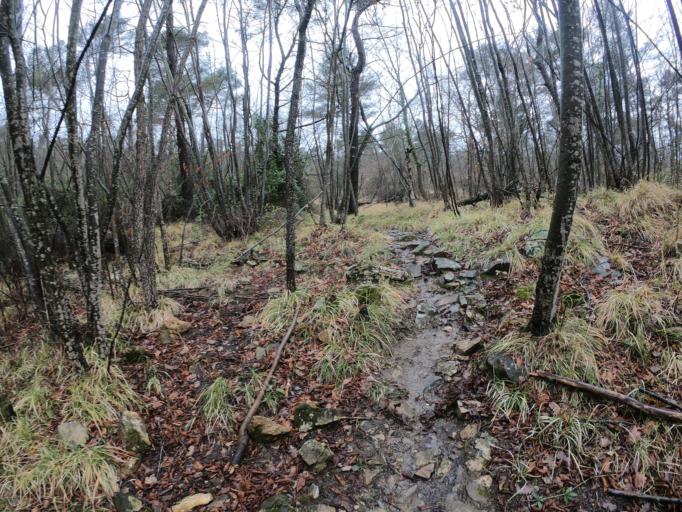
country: IT
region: Liguria
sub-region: Provincia di Imperia
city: Villa Faraldi
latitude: 43.9756
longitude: 8.1040
